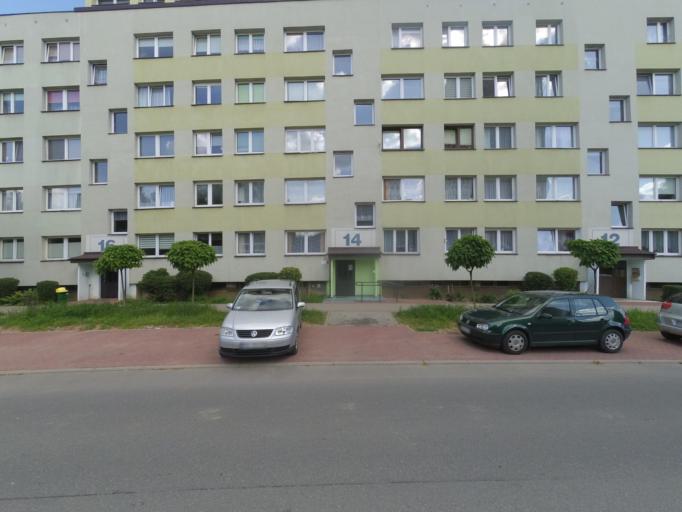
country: PL
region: Lower Silesian Voivodeship
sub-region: Powiat klodzki
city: Klodzko
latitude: 50.4323
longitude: 16.6433
